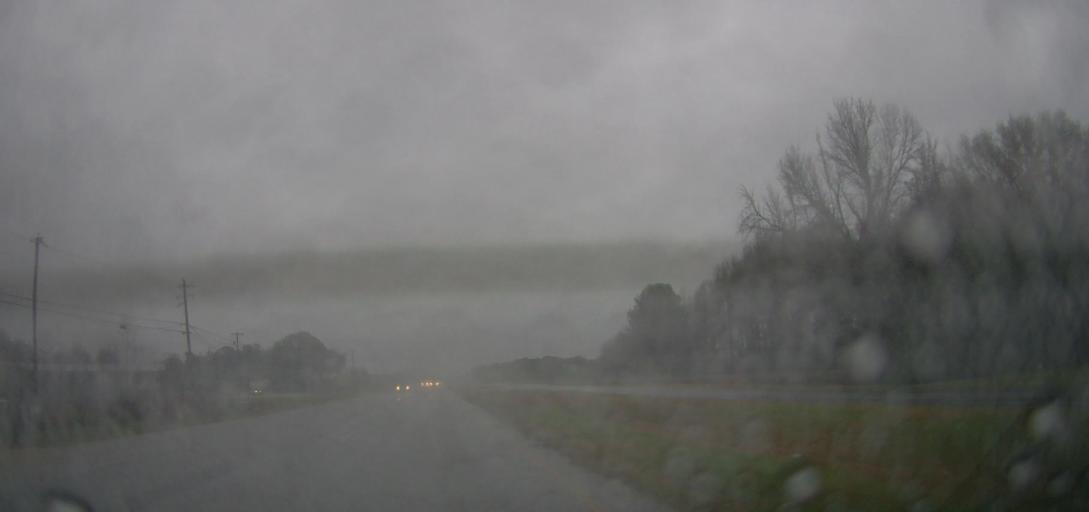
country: US
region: Alabama
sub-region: Montgomery County
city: Montgomery
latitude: 32.3875
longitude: -86.3848
